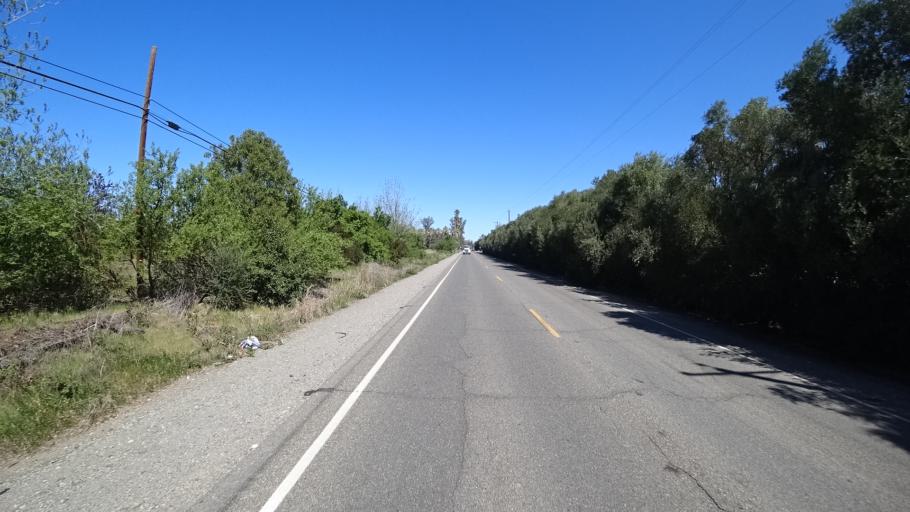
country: US
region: California
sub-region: Glenn County
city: Orland
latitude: 39.7047
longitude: -122.1969
